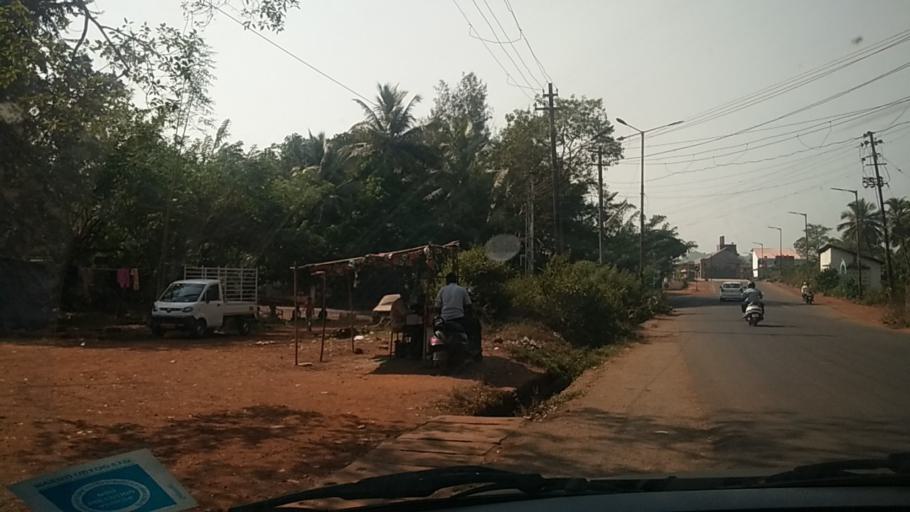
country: IN
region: Goa
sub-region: North Goa
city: Dicholi
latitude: 15.5878
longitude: 73.9520
